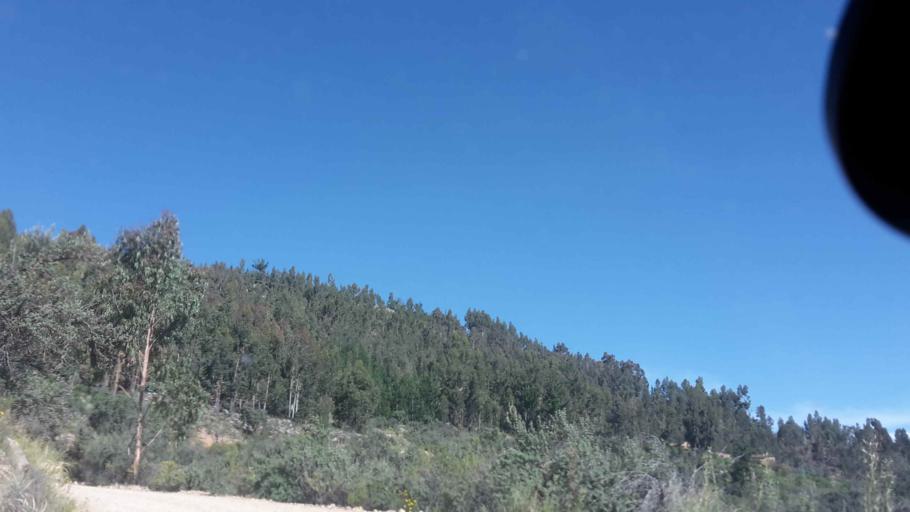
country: BO
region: Cochabamba
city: Arani
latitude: -17.6703
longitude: -65.7301
